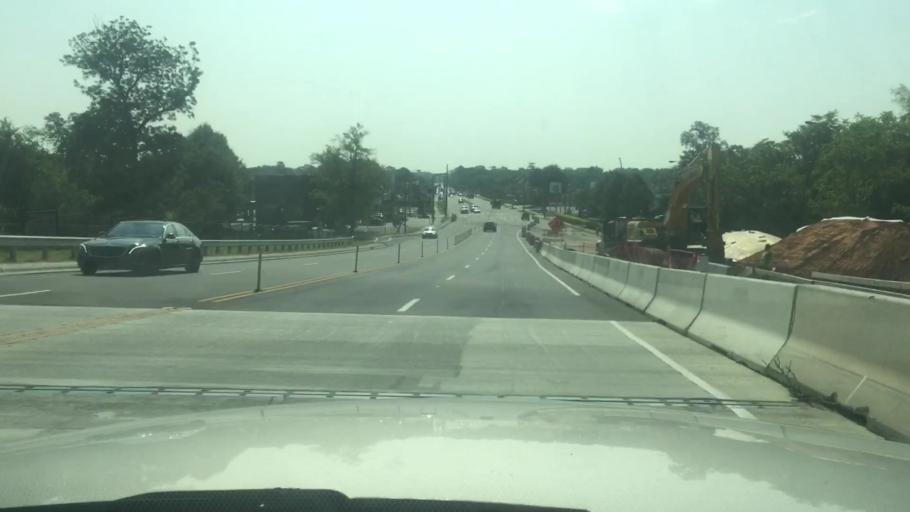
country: US
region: North Carolina
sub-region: Cumberland County
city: Fayetteville
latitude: 35.0594
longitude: -78.8825
